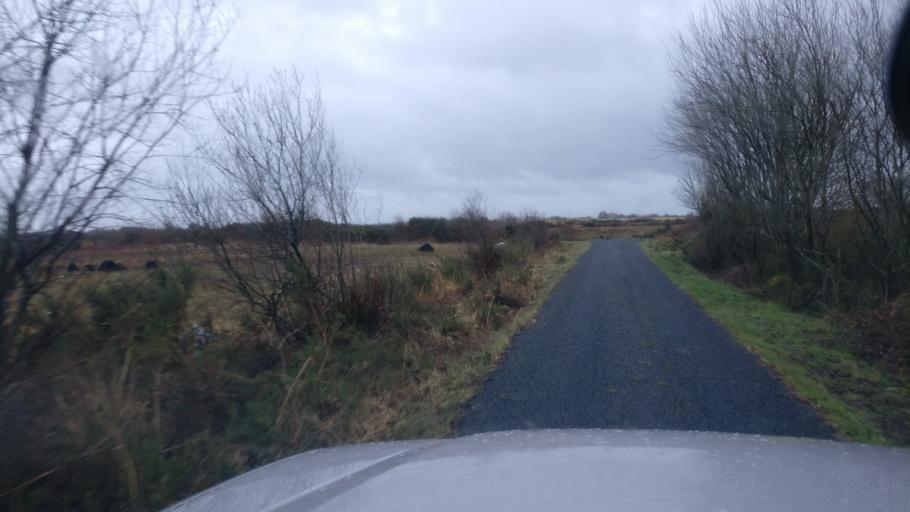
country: IE
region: Connaught
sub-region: County Galway
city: Ballinasloe
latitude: 53.2456
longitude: -8.3271
